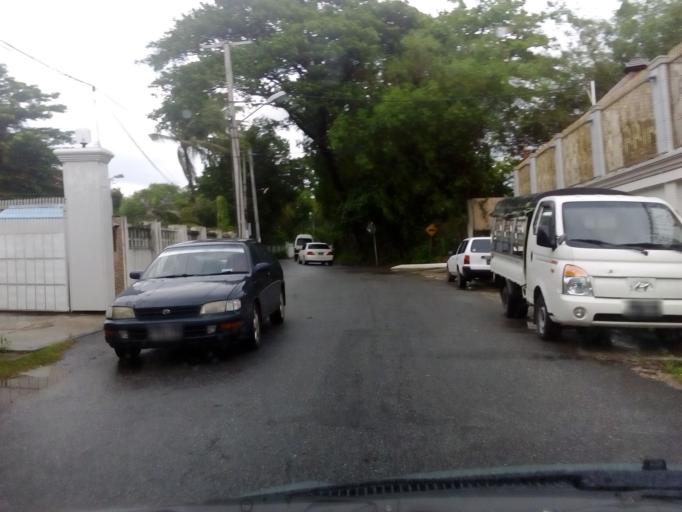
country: MM
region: Yangon
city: Yangon
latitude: 16.8160
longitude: 96.1479
